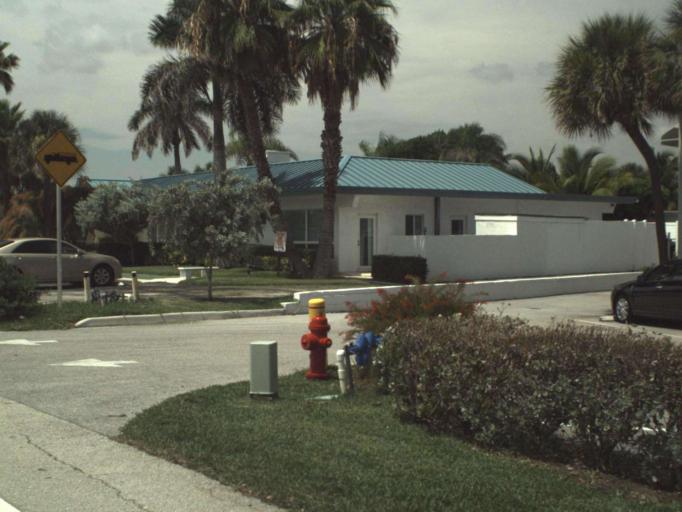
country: US
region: Florida
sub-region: Broward County
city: Hillsboro Beach
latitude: 26.3019
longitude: -80.0781
